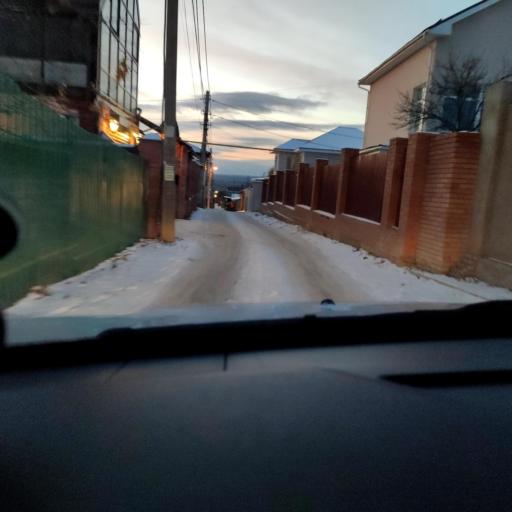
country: RU
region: Samara
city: Samara
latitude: 53.2584
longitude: 50.1998
